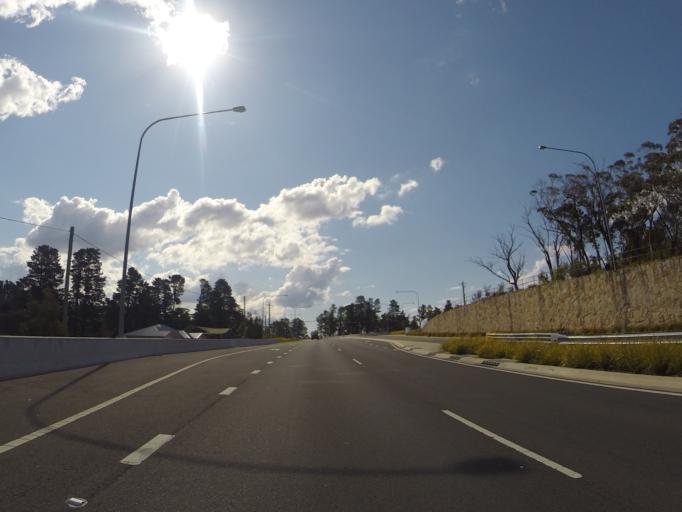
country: AU
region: New South Wales
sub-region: Blue Mountains Municipality
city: Lawson
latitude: -33.7184
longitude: 150.3828
